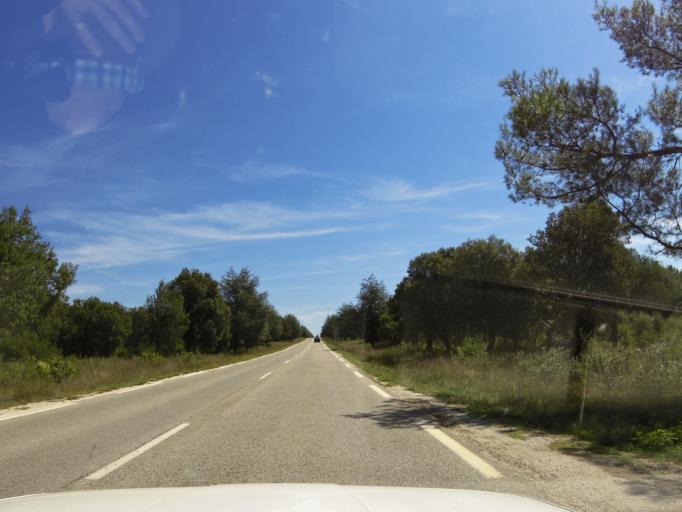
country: FR
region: Languedoc-Roussillon
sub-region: Departement du Gard
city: Saint-Quentin-la-Poterie
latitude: 44.1294
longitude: 4.4381
